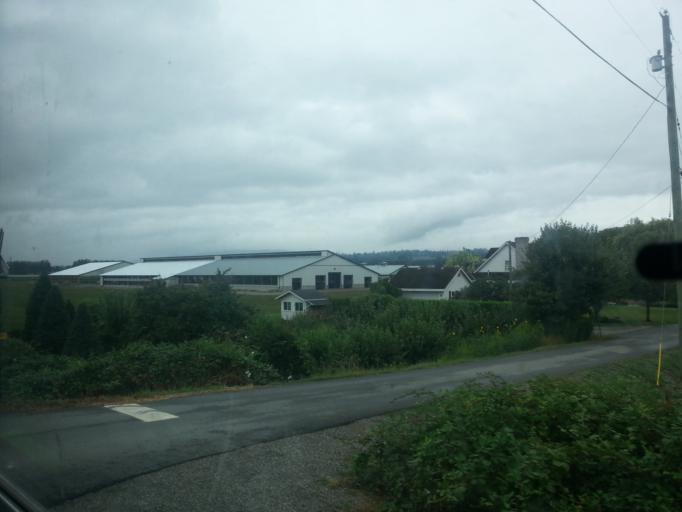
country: CA
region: British Columbia
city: Abbotsford
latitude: 49.1165
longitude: -122.2657
